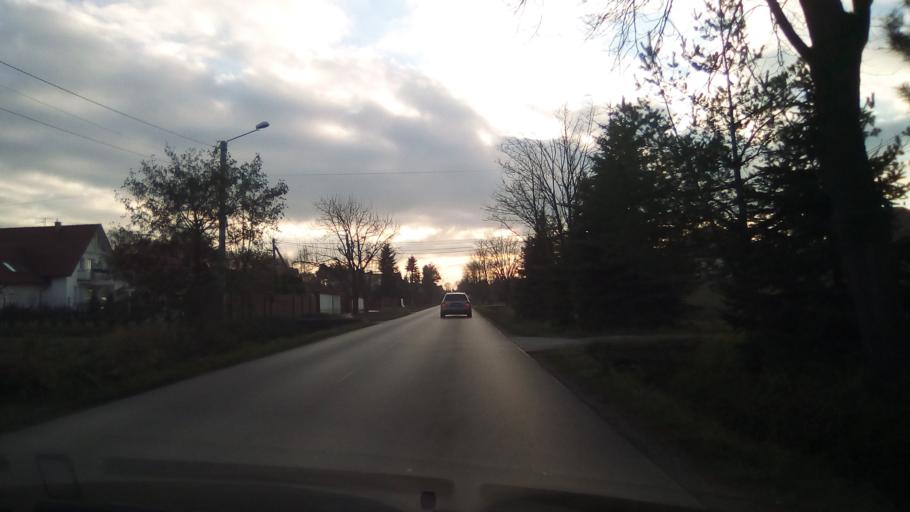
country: PL
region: Subcarpathian Voivodeship
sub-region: Rzeszow
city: Przybyszowka
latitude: 50.0350
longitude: 21.8956
